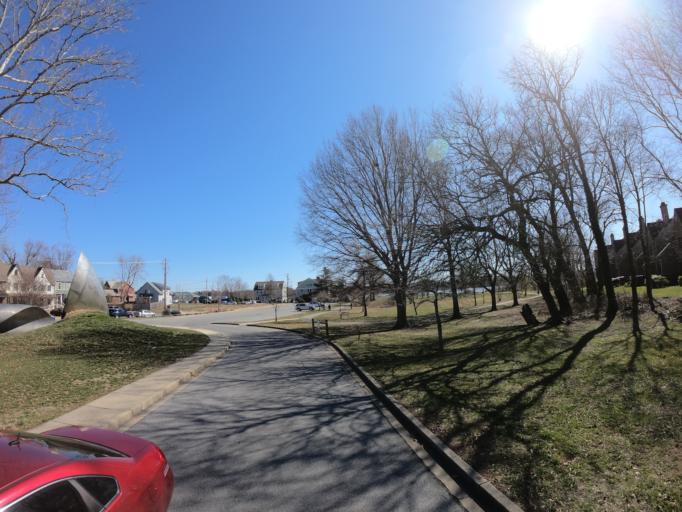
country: US
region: Maryland
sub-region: Kent County
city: Chestertown
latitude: 39.2058
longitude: -76.0672
